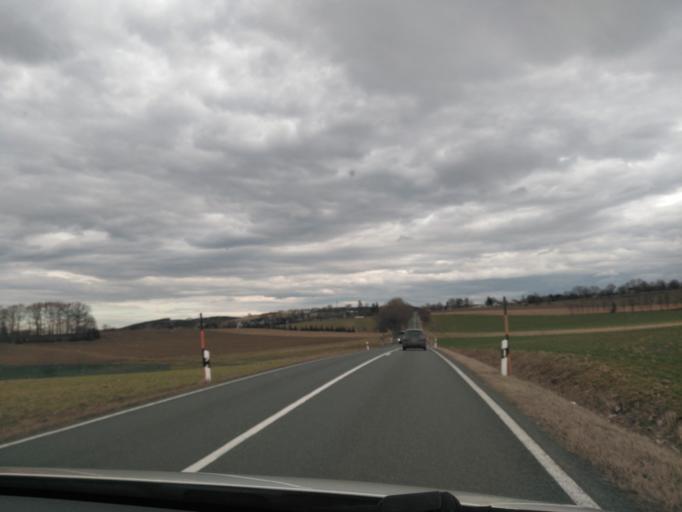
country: DE
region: Saxony
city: Wolkenstein
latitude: 50.6674
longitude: 13.1032
